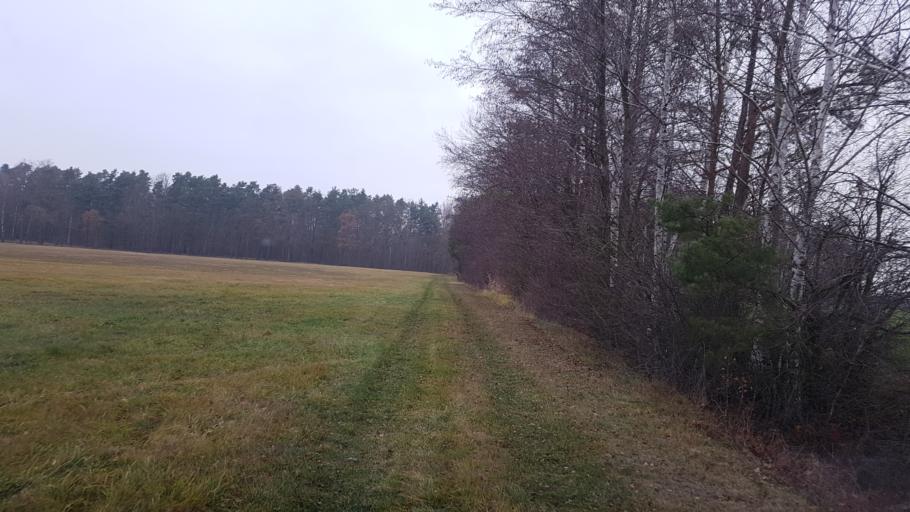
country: DE
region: Brandenburg
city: Doberlug-Kirchhain
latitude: 51.6291
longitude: 13.5349
